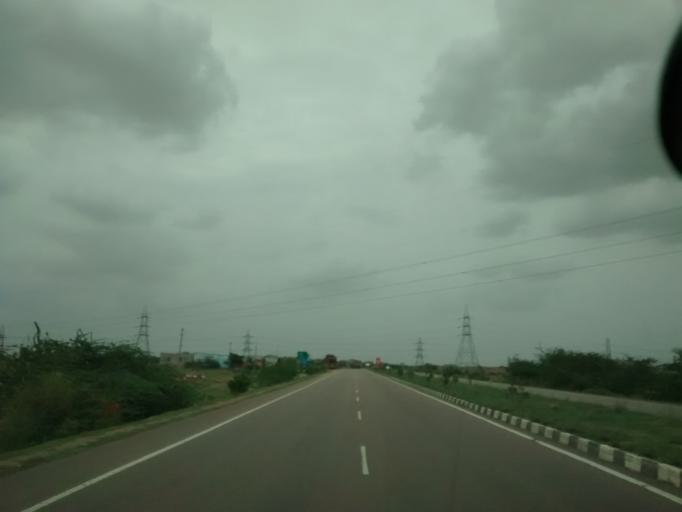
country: IN
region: Andhra Pradesh
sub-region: Kurnool
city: Ramapuram
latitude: 15.1447
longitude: 77.6645
